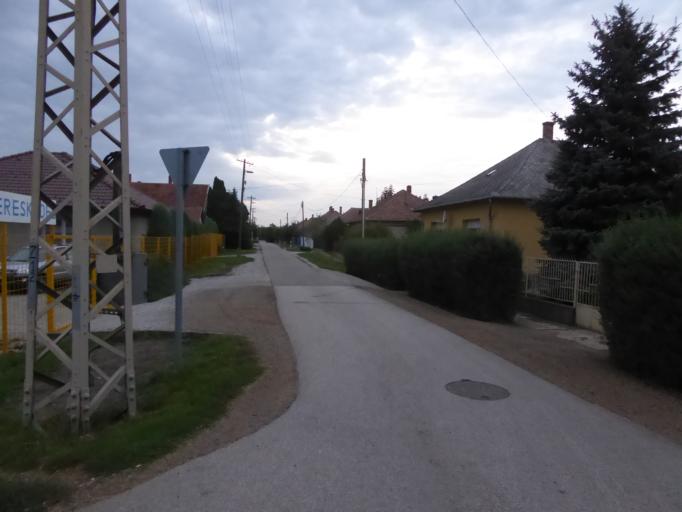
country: HU
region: Jasz-Nagykun-Szolnok
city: Jaszapati
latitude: 47.5236
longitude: 20.1583
